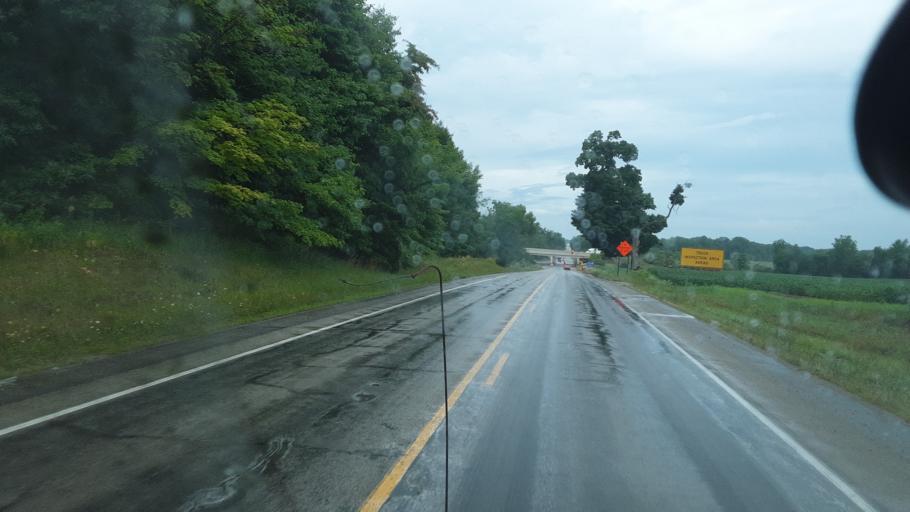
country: US
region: Indiana
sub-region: Steuben County
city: Hamilton
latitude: 41.6307
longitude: -84.8133
